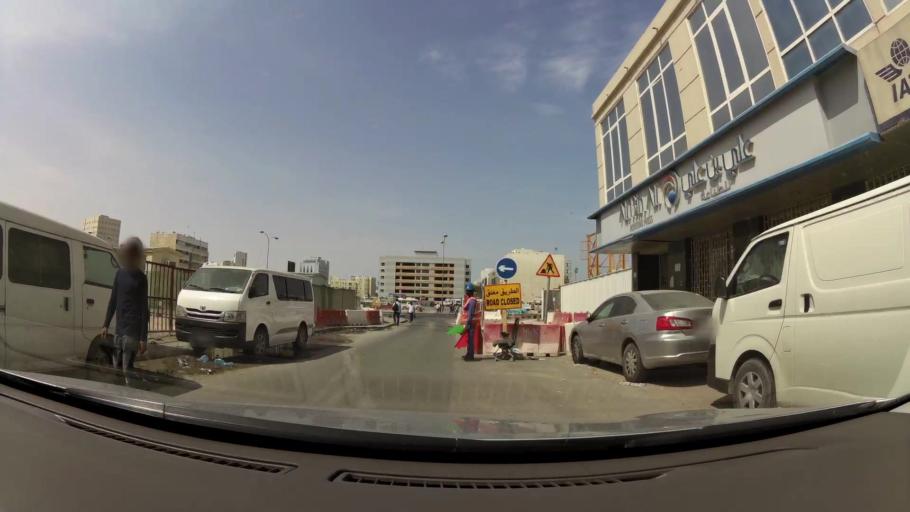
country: QA
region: Baladiyat ad Dawhah
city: Doha
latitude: 25.2792
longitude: 51.5342
